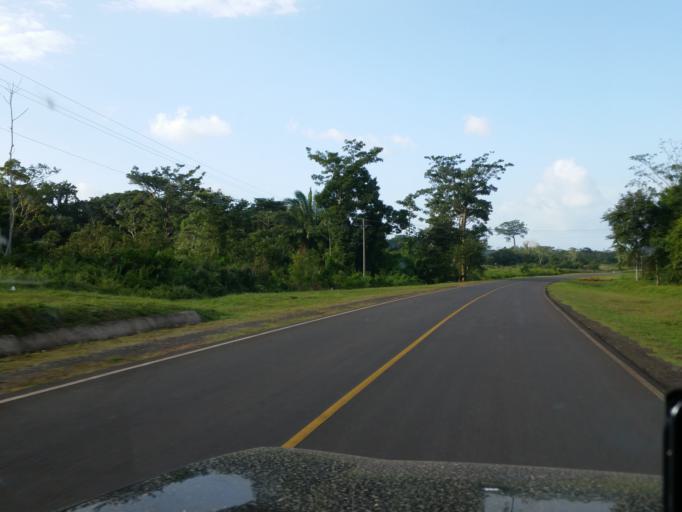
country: NI
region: Rio San Juan
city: San Carlos
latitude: 11.1782
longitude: -84.6782
